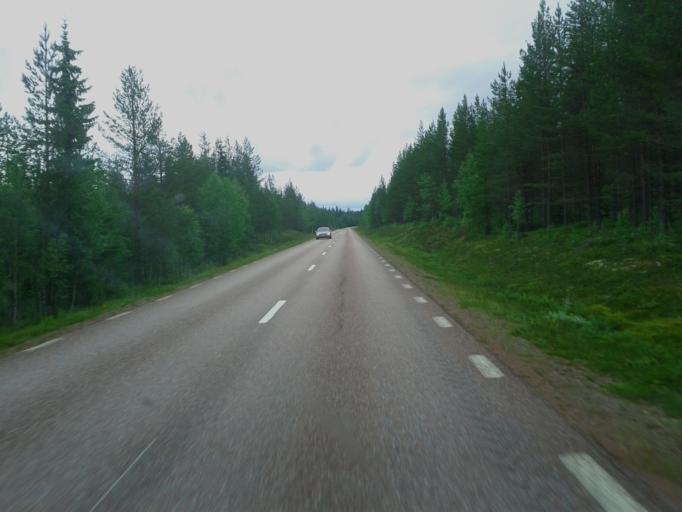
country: NO
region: Hedmark
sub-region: Trysil
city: Innbygda
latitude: 61.7079
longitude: 13.0149
